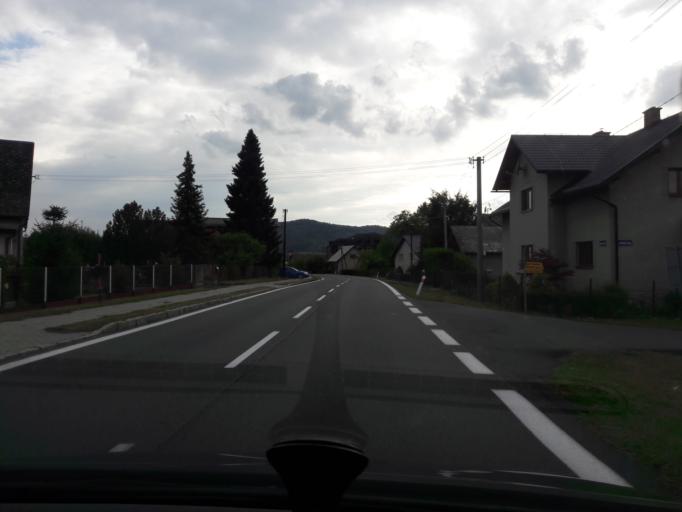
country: CZ
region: Olomoucky
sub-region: Okres Sumperk
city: Velke Losiny
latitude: 50.0349
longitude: 17.0446
